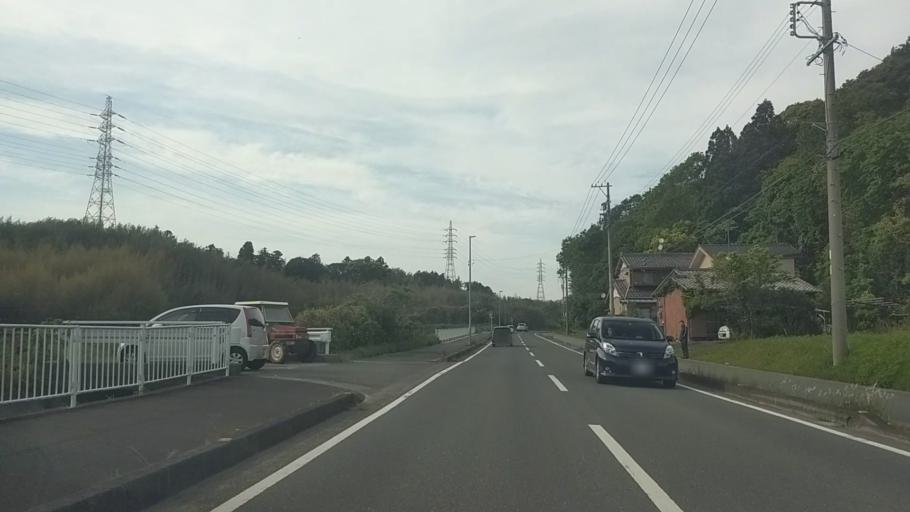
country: JP
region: Shizuoka
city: Hamamatsu
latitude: 34.7484
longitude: 137.6541
